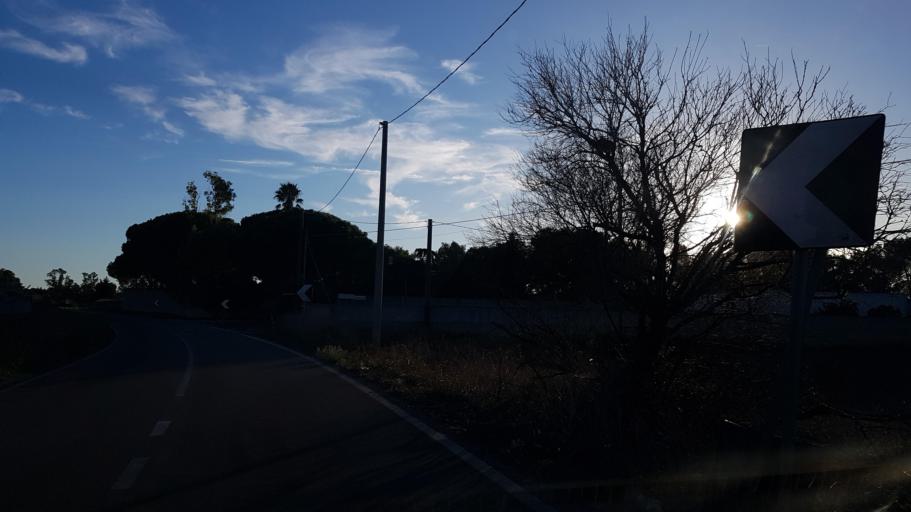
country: IT
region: Apulia
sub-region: Provincia di Lecce
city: Giorgilorio
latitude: 40.4067
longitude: 18.1993
